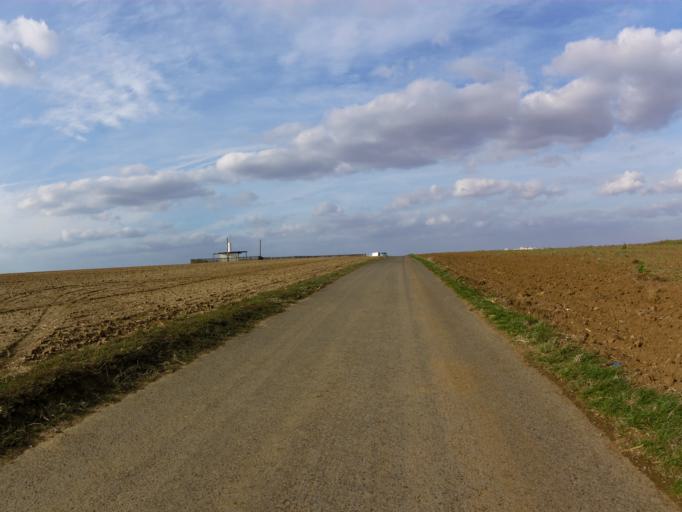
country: DE
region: Bavaria
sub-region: Regierungsbezirk Unterfranken
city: Reichenberg
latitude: 49.7164
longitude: 9.9478
